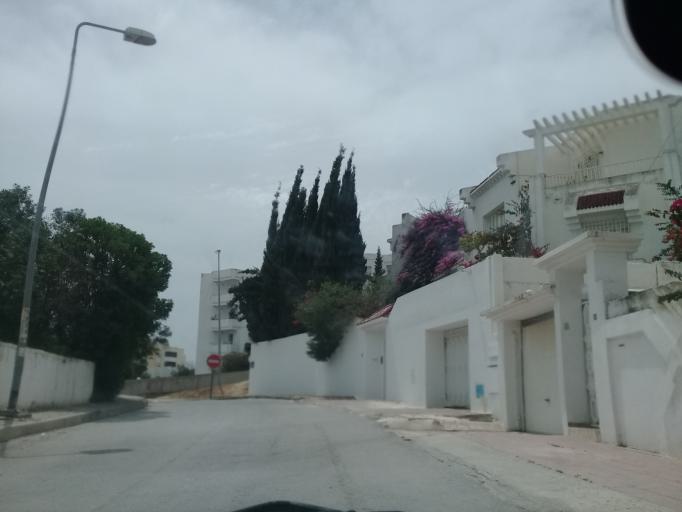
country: TN
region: Tunis
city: Tunis
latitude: 36.8370
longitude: 10.1532
